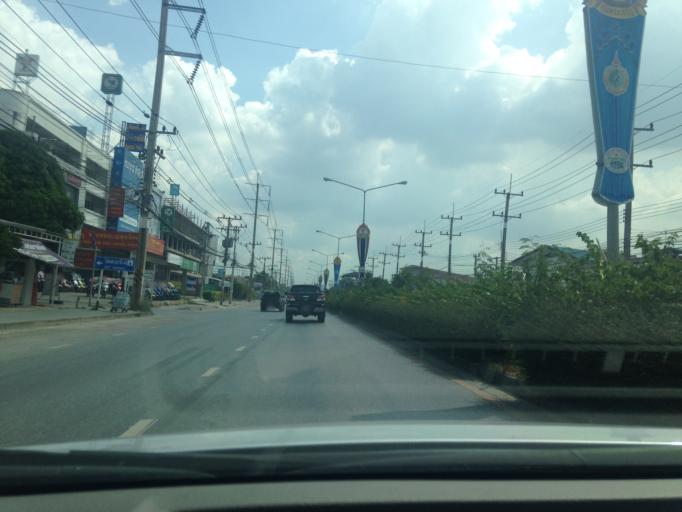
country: TH
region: Pathum Thani
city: Sam Khok
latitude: 14.0666
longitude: 100.5235
